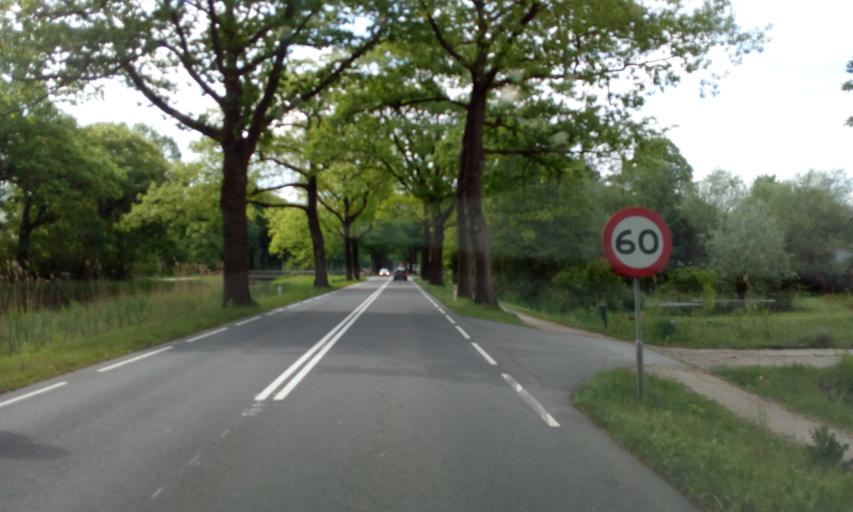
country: NL
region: Gelderland
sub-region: Gemeente Apeldoorn
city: Beekbergen
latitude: 52.1723
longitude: 5.9966
